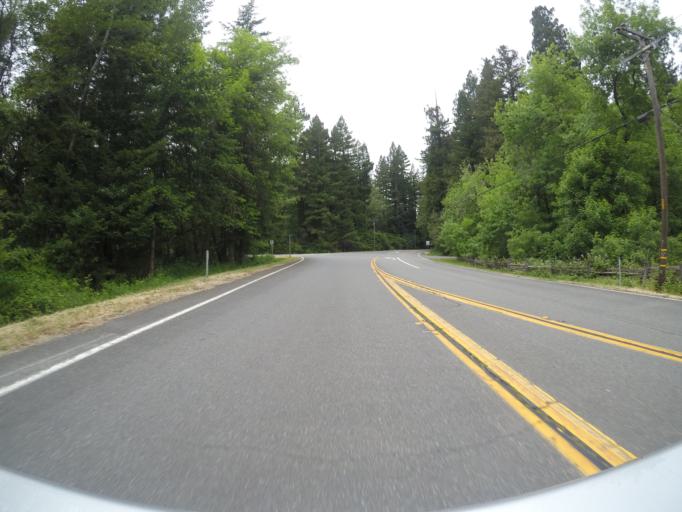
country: US
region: California
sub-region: Humboldt County
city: Rio Dell
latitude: 40.3984
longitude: -123.9465
